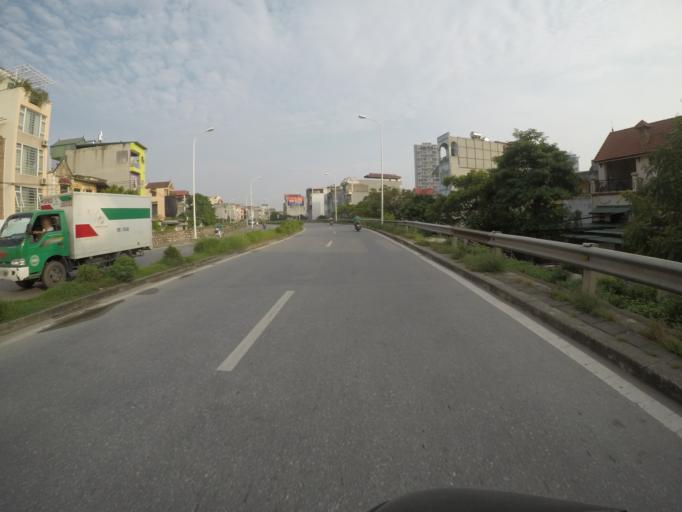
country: VN
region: Ha Noi
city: Tay Ho
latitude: 21.0892
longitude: 105.8133
